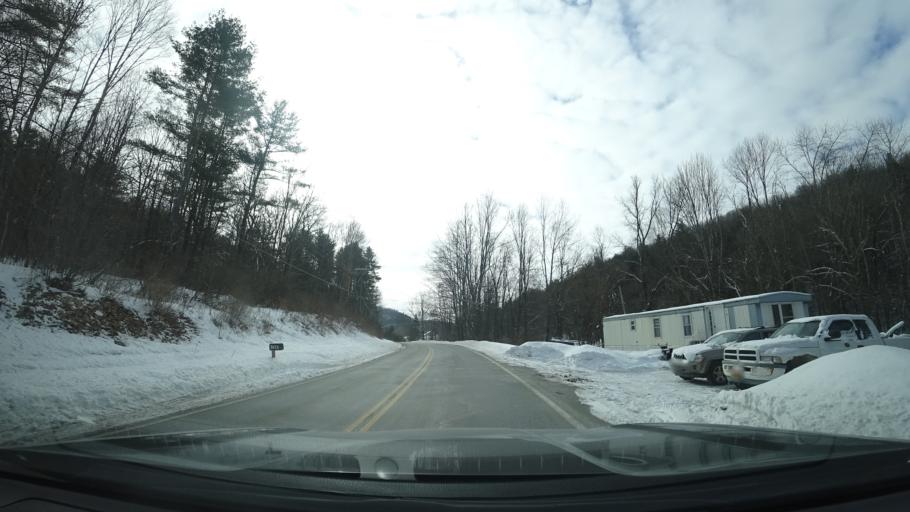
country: US
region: New York
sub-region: Washington County
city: Greenwich
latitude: 43.2355
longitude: -73.3778
